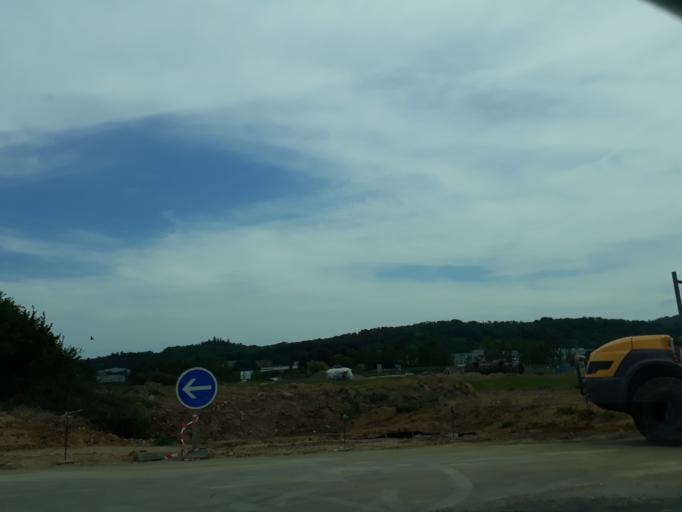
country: FR
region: Limousin
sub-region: Departement de la Correze
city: Saint-Pantaleon-de-Larche
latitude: 45.1483
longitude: 1.4785
